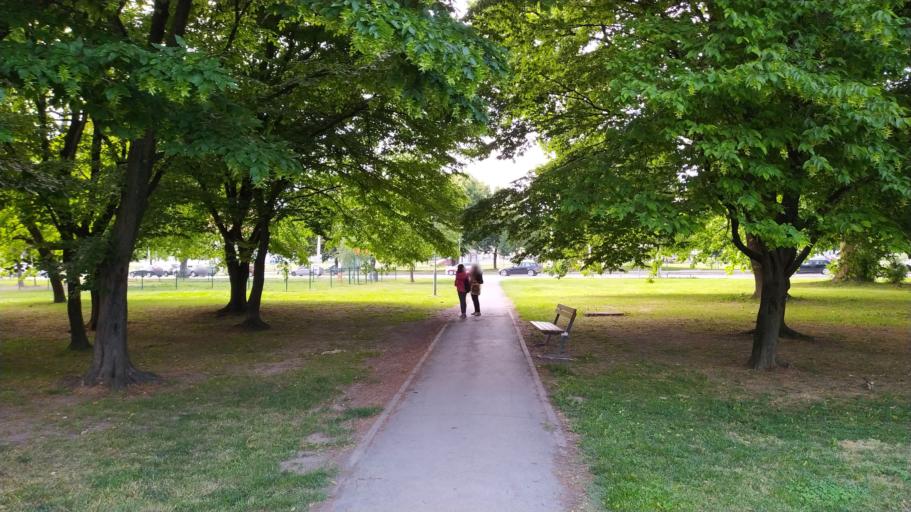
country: HR
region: Osjecko-Baranjska
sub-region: Grad Osijek
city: Osijek
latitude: 45.5581
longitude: 18.6995
